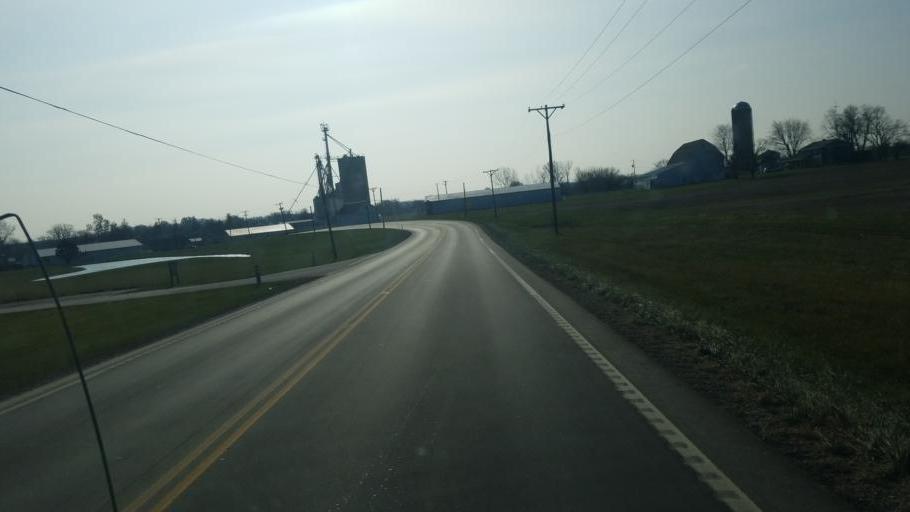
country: US
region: Ohio
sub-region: Mercer County
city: Fort Recovery
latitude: 40.4200
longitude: -84.7847
